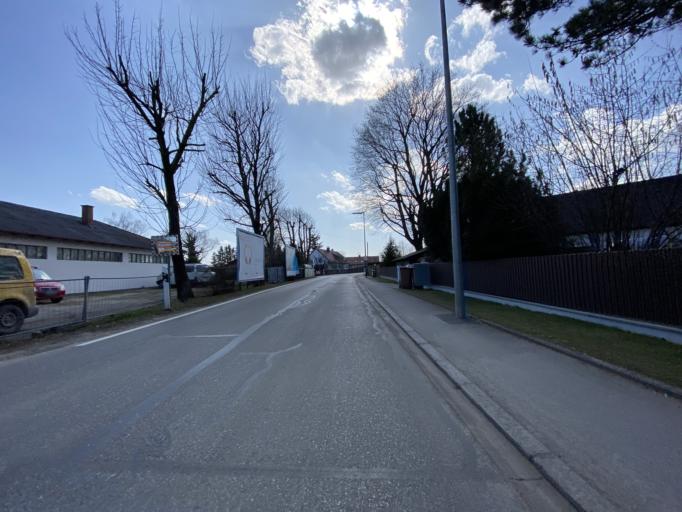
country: DE
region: Bavaria
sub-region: Upper Bavaria
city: Unterfoehring
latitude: 48.1611
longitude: 11.6625
